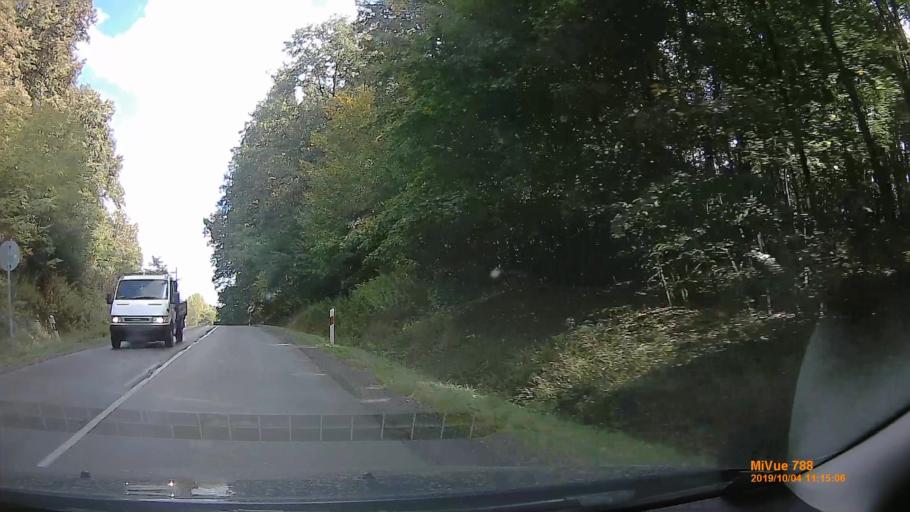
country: HU
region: Somogy
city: Kaposvar
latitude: 46.4435
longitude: 17.7996
